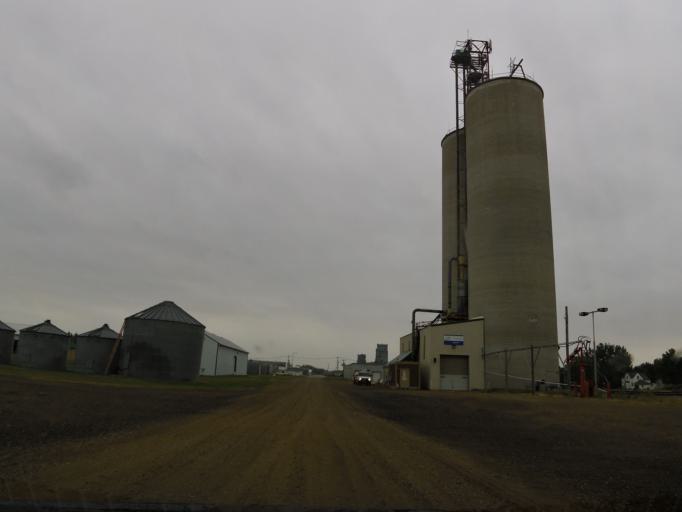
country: US
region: Minnesota
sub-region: Marshall County
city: Warren
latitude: 48.4560
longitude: -96.8748
